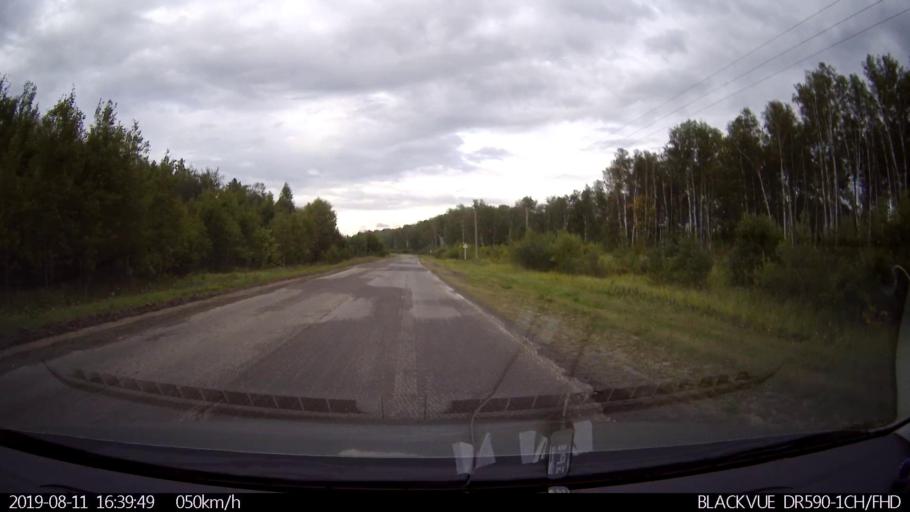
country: RU
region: Ulyanovsk
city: Mayna
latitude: 54.1421
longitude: 47.6404
